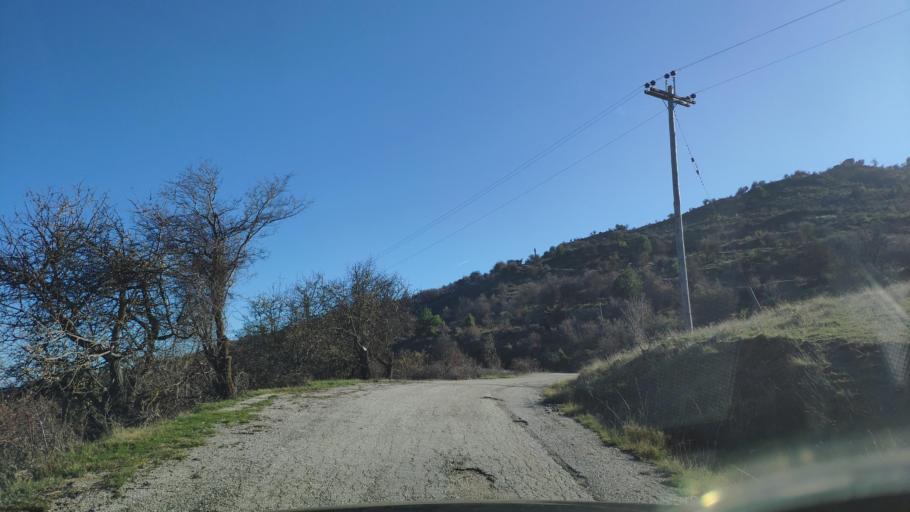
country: GR
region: West Greece
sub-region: Nomos Achaias
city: Aiyira
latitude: 38.0409
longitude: 22.4617
